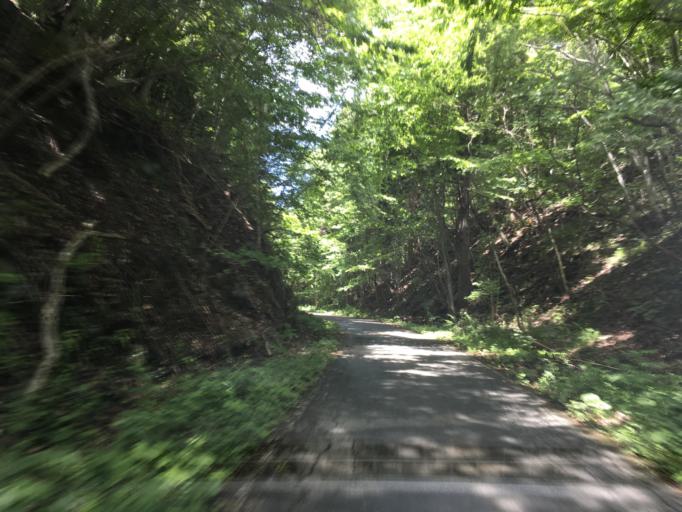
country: JP
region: Iwate
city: Mizusawa
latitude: 39.1260
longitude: 141.2655
